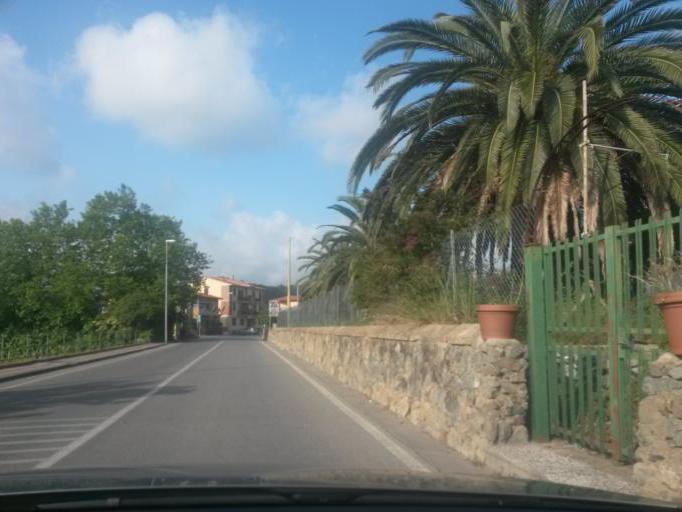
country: IT
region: Tuscany
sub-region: Provincia di Livorno
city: Porto Azzurro
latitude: 42.7711
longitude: 10.3993
